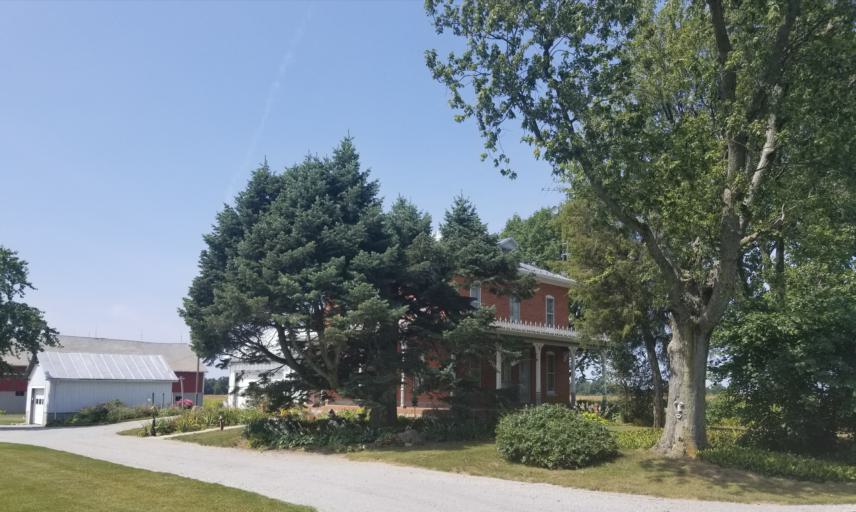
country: US
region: Ohio
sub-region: Crawford County
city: Bucyrus
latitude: 40.8965
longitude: -83.0741
